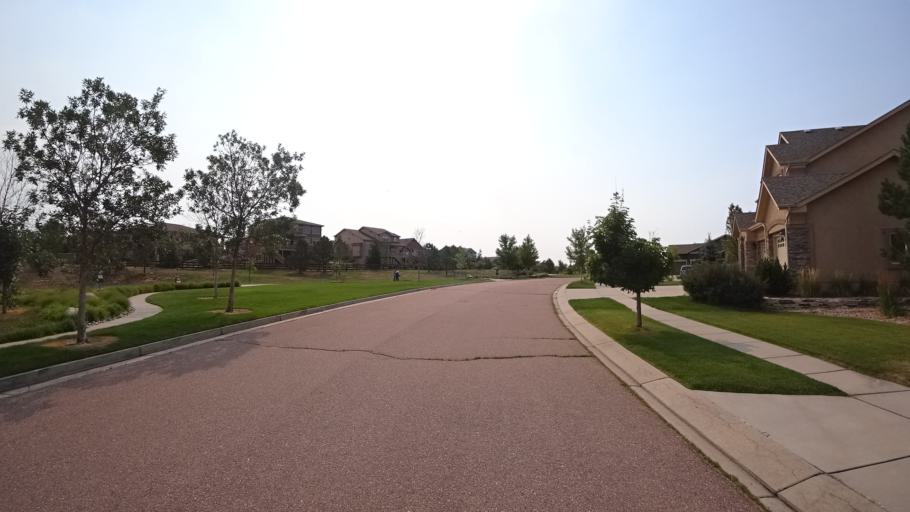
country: US
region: Colorado
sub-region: El Paso County
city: Black Forest
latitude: 38.9702
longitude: -104.7361
